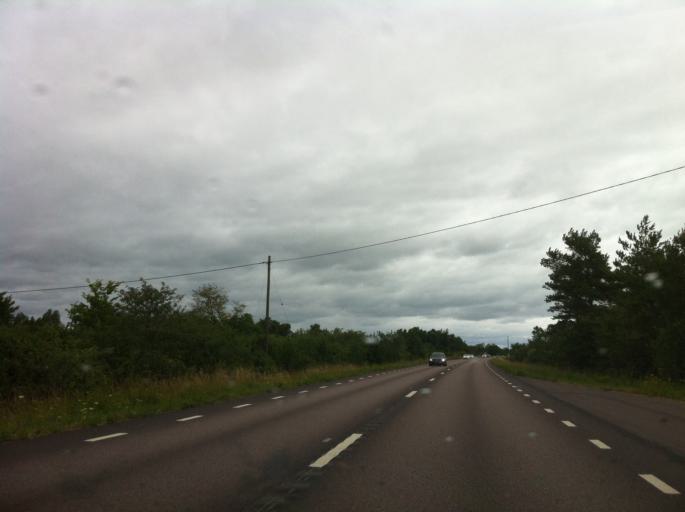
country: SE
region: Kalmar
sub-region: Borgholms Kommun
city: Borgholm
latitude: 57.0976
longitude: 16.9300
